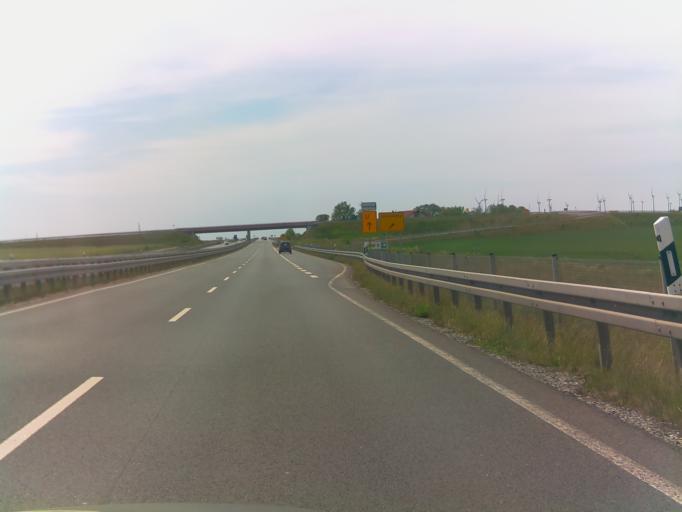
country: DE
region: Saxony-Anhalt
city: Wolmirsleben
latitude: 52.0046
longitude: 11.4981
